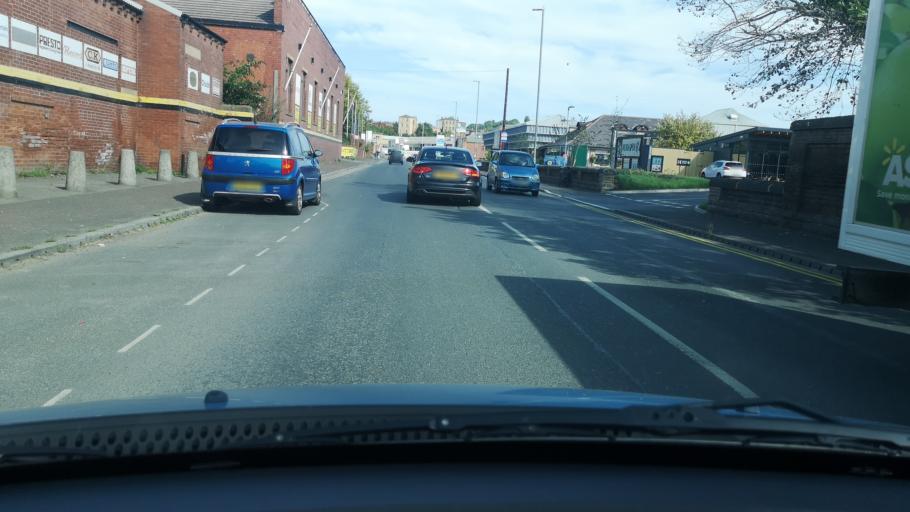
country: GB
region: England
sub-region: Kirklees
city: Batley
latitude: 53.7055
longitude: -1.6278
